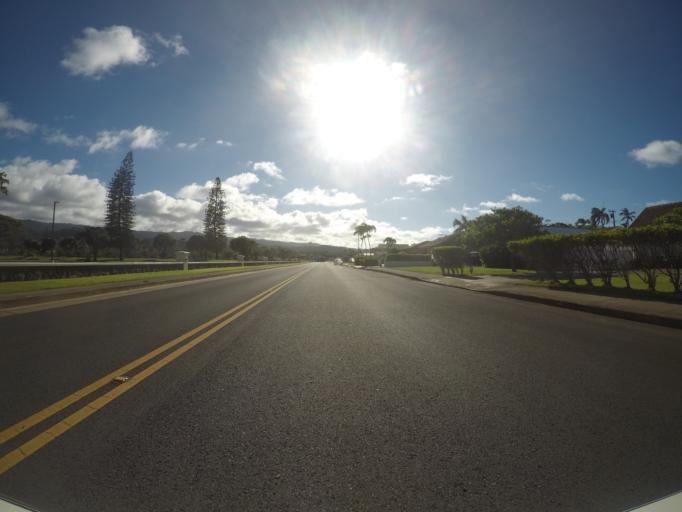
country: US
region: Hawaii
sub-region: Honolulu County
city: La'ie
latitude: 21.6443
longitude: -157.9233
